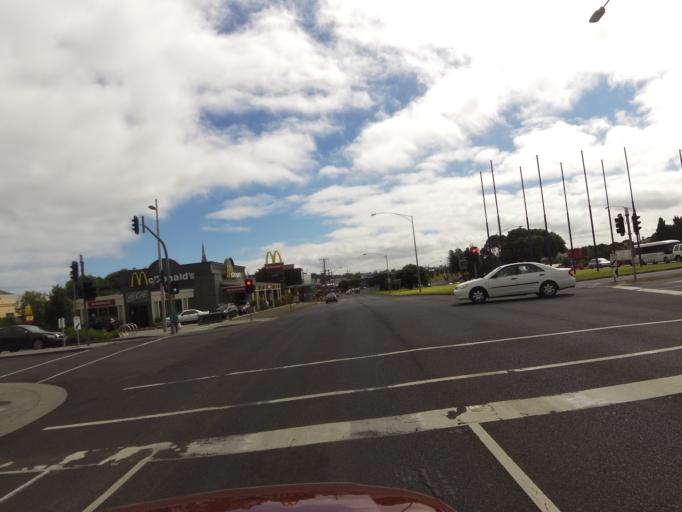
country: AU
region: Victoria
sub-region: Warrnambool
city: Warrnambool
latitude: -38.3809
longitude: 142.4859
